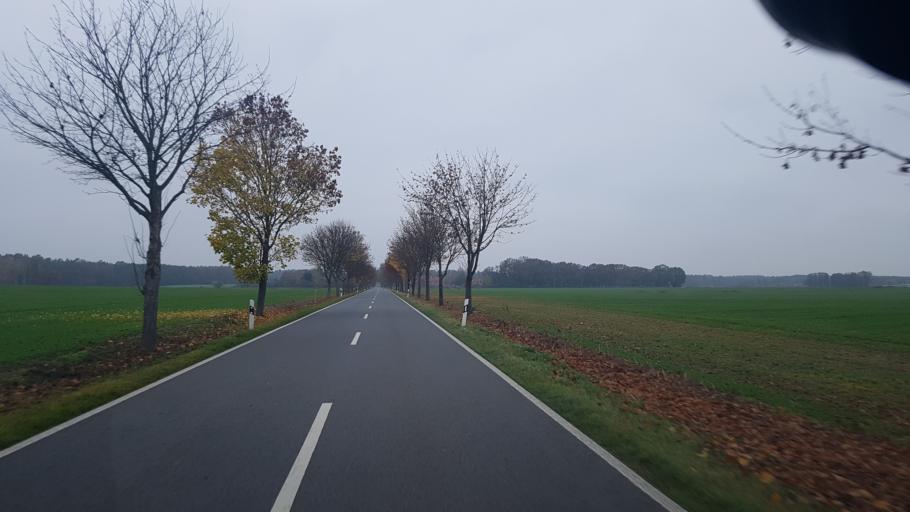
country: DE
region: Brandenburg
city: Lindow
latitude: 52.9459
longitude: 13.0121
